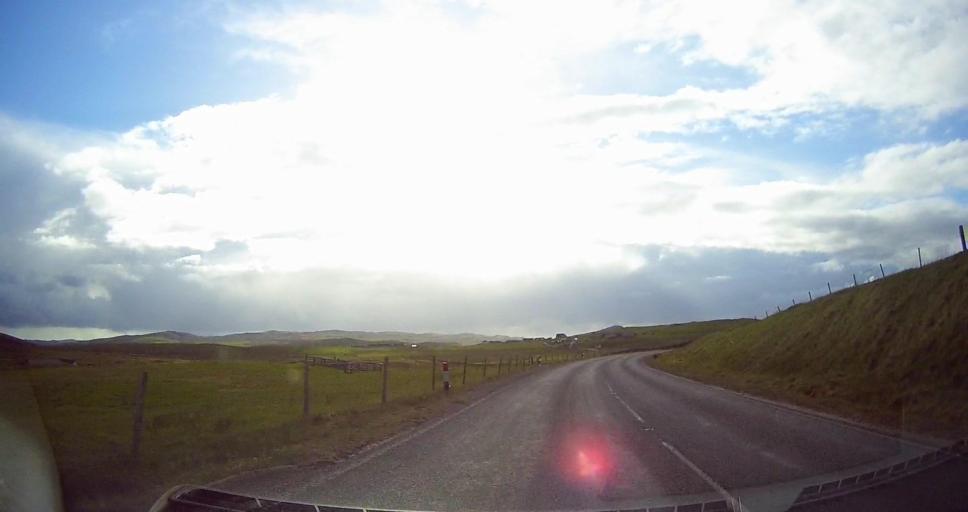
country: GB
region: Scotland
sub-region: Shetland Islands
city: Lerwick
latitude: 60.3706
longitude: -1.3294
